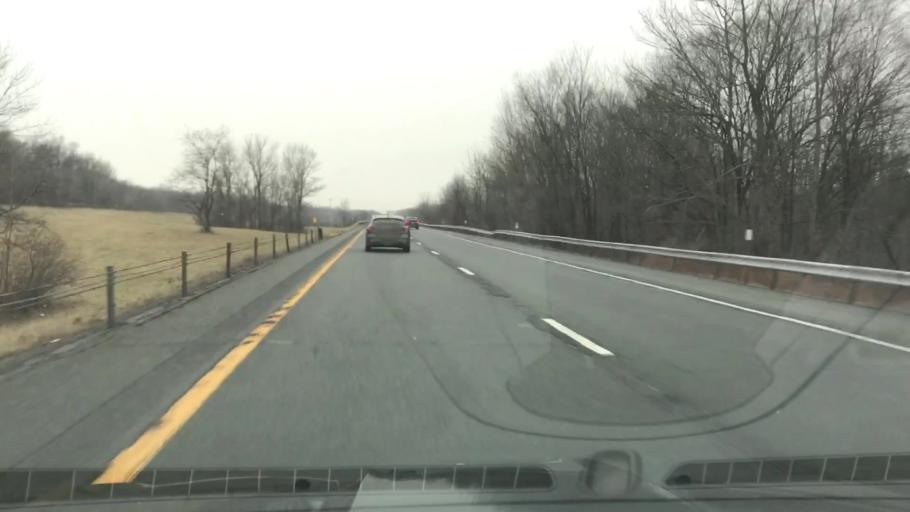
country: US
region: New York
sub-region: Orange County
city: Otisville
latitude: 41.3957
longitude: -74.5497
